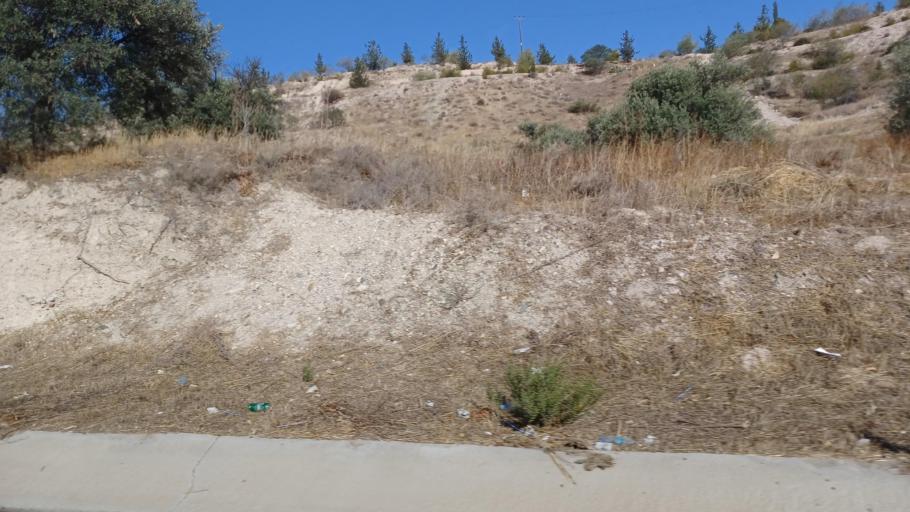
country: CY
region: Lefkosia
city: Alampra
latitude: 35.0028
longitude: 33.3817
